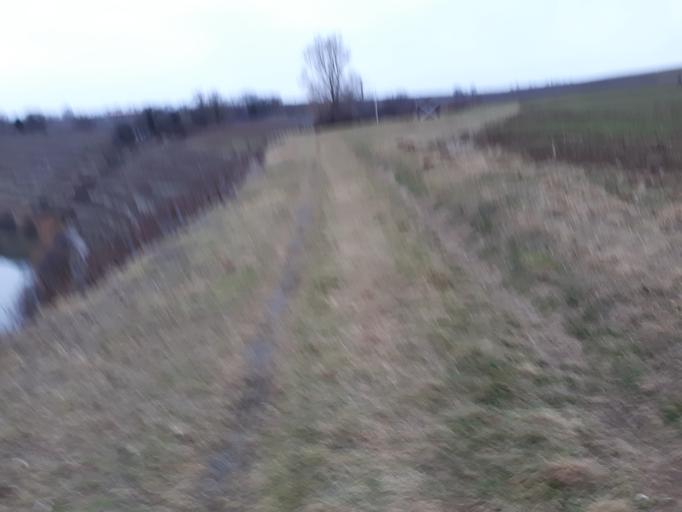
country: DE
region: Baden-Wuerttemberg
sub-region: Regierungsbezirk Stuttgart
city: Kirchheim am Neckar
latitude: 49.0495
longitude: 9.1588
